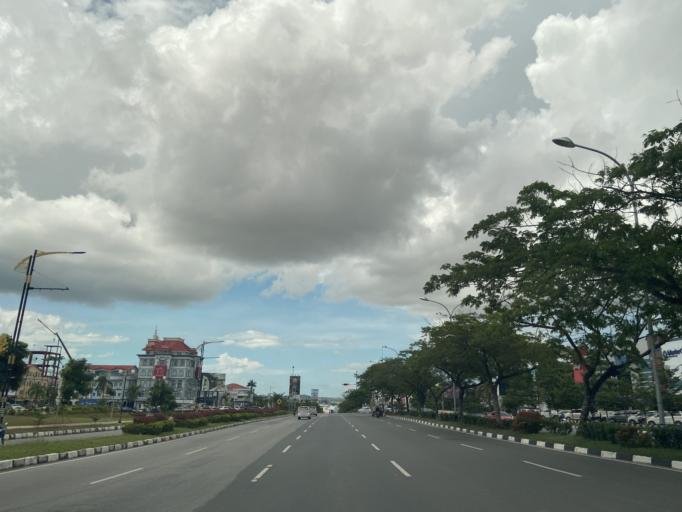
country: SG
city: Singapore
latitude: 1.1259
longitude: 104.0303
